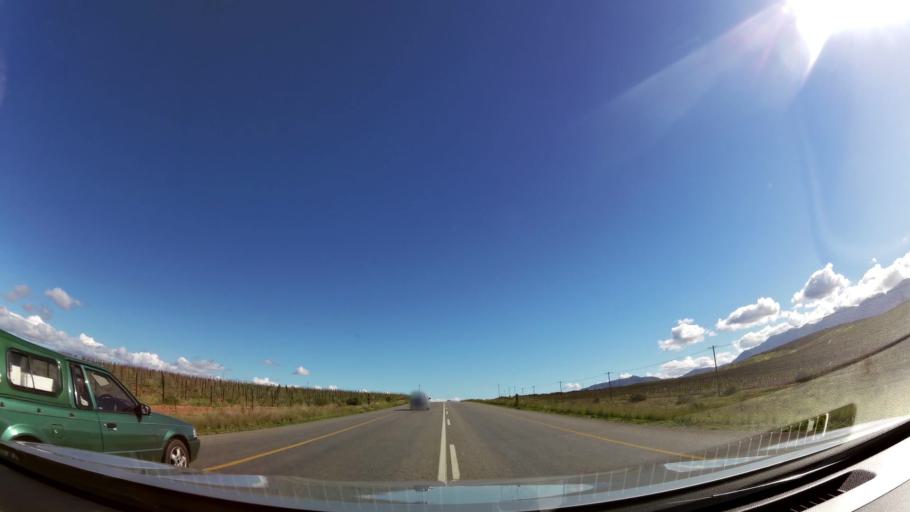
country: ZA
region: Western Cape
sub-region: Cape Winelands District Municipality
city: Ashton
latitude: -33.8182
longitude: 19.9630
